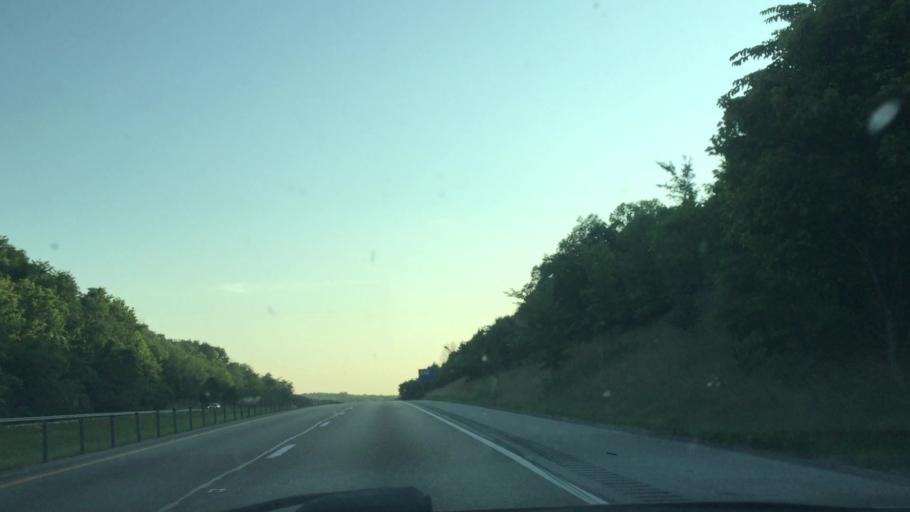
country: US
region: Kentucky
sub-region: Gallatin County
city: Warsaw
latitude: 38.7468
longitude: -84.8237
